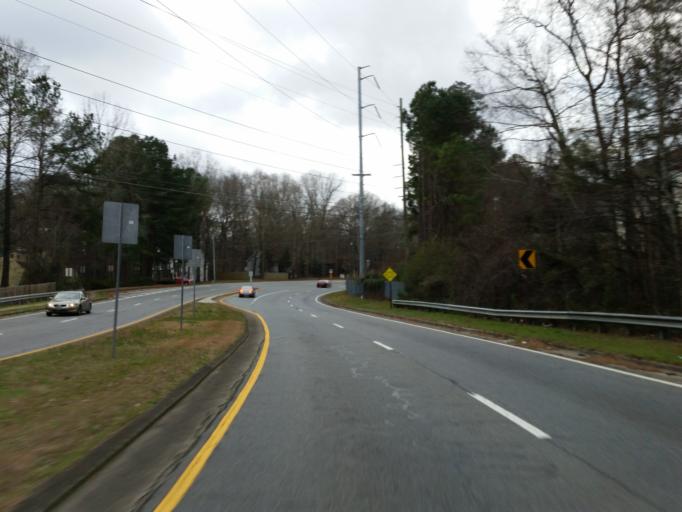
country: US
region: Georgia
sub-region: Cherokee County
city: Woodstock
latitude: 34.0355
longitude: -84.5438
